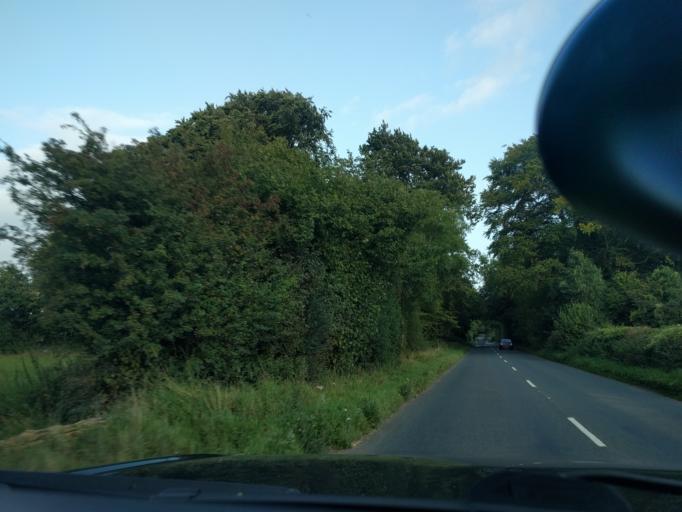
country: GB
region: England
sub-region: Wiltshire
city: Neston
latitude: 51.4025
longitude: -2.2211
